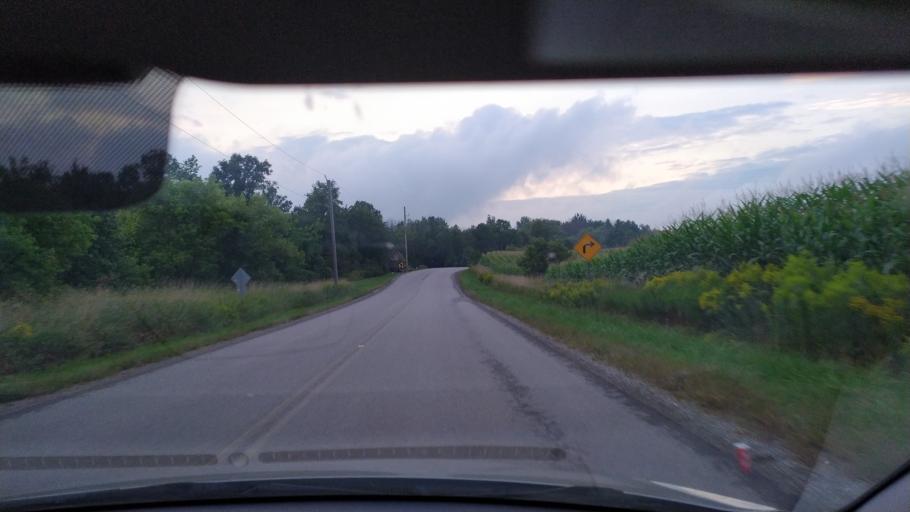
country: CA
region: Ontario
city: Kitchener
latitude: 43.3471
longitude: -80.6382
